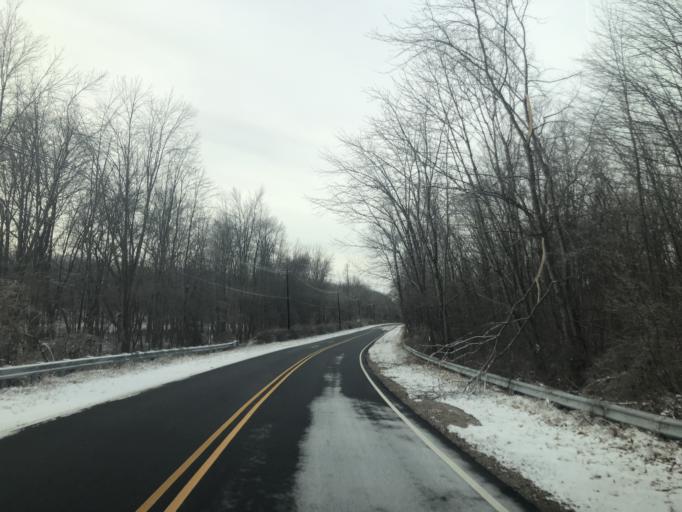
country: US
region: New Jersey
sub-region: Warren County
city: Belvidere
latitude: 40.9337
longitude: -75.0271
